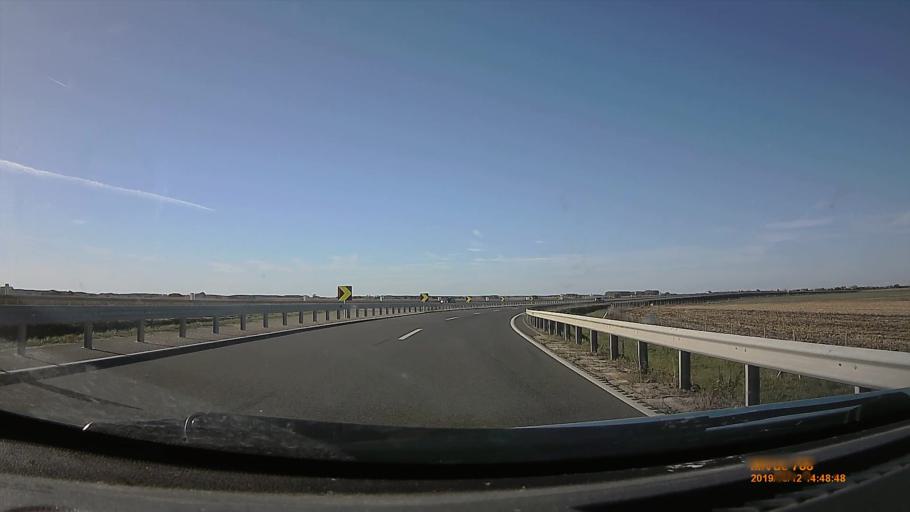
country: HU
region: Hajdu-Bihar
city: Derecske
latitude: 47.2931
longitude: 21.5071
